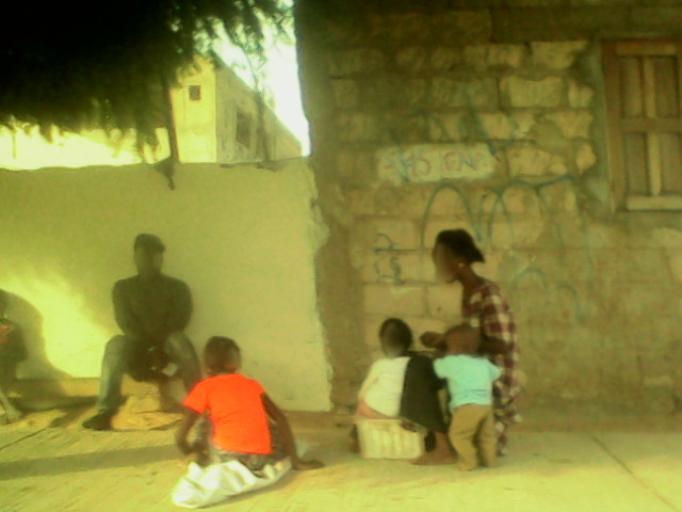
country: SN
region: Diourbel
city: Touba
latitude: 14.8621
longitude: -15.8692
